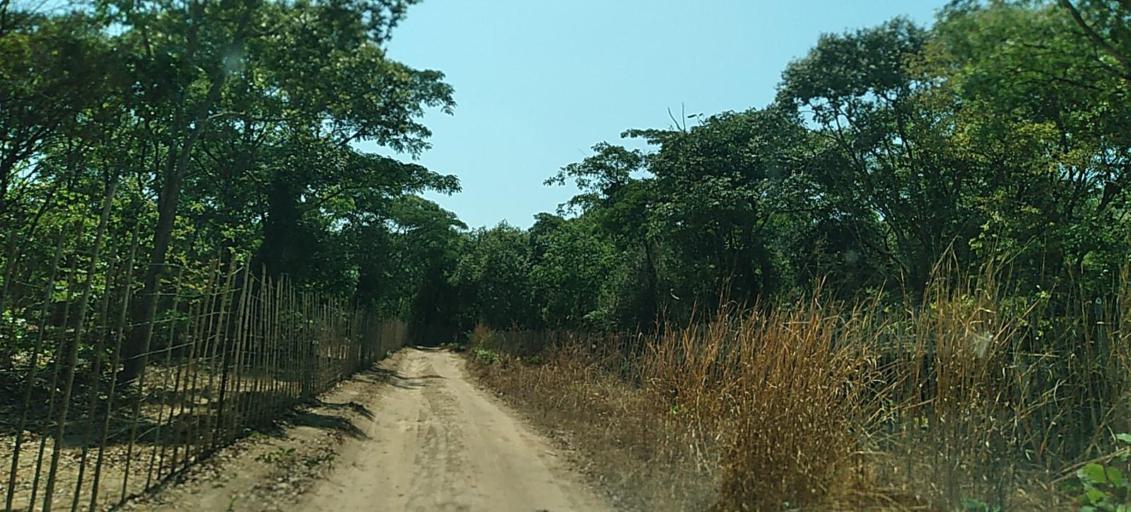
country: ZM
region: Copperbelt
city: Luanshya
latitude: -13.0097
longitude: 28.4656
